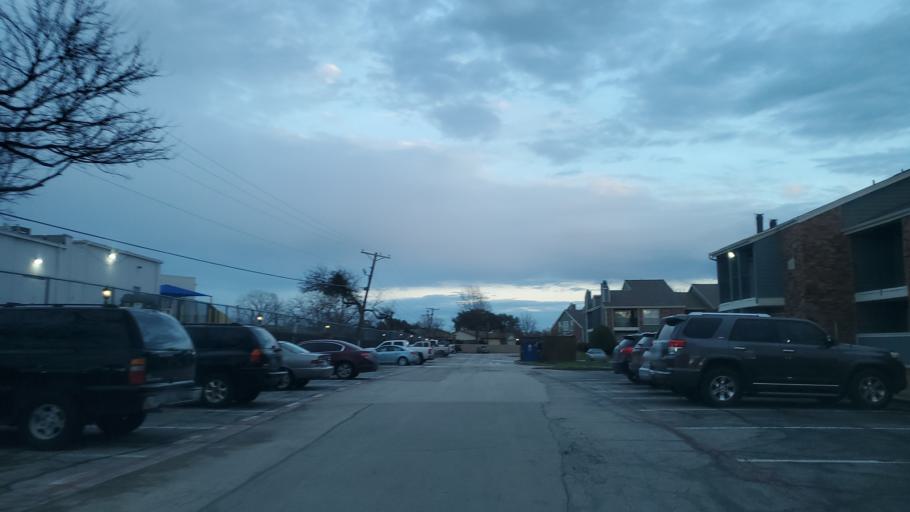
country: US
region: Texas
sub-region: Dallas County
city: Carrollton
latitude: 32.9966
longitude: -96.8857
